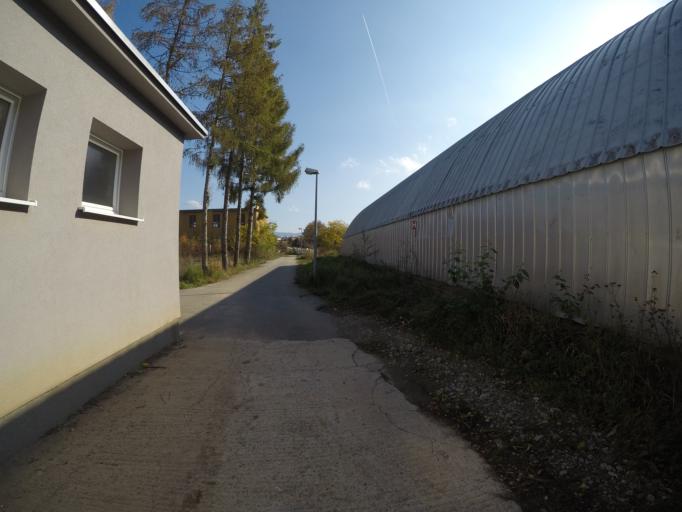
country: SK
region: Trenciansky
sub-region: Okres Nove Mesto nad Vahom
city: Nove Mesto nad Vahom
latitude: 48.7635
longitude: 17.8211
